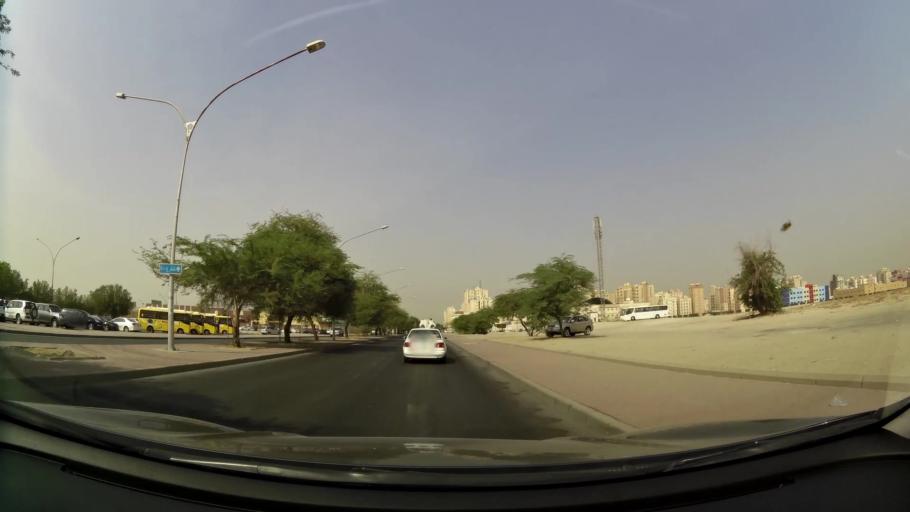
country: KW
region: Al Farwaniyah
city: Al Farwaniyah
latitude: 29.2496
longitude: 47.9305
